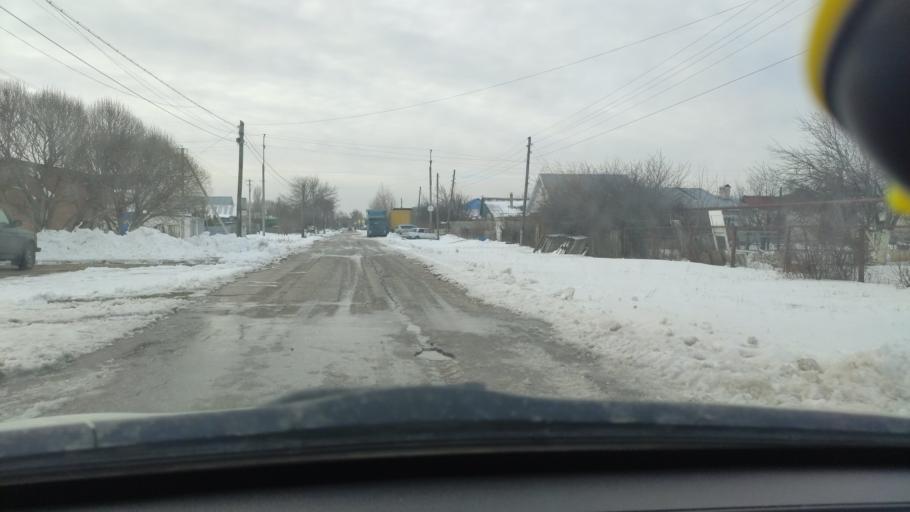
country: RU
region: Samara
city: Tol'yatti
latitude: 53.5668
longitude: 49.3941
